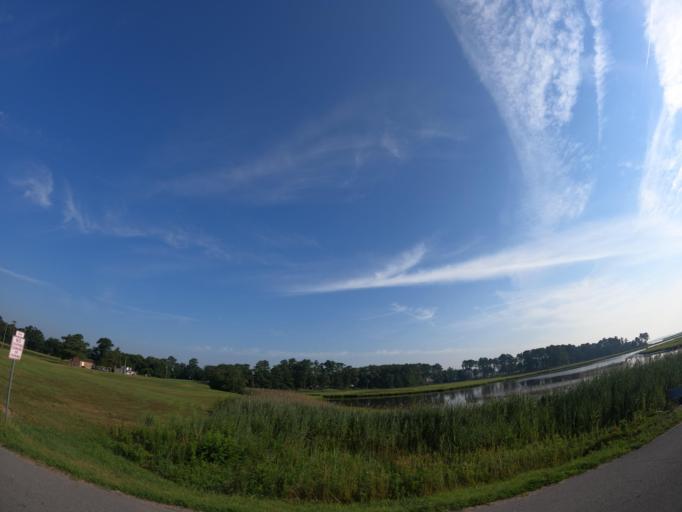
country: US
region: Delaware
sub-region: Sussex County
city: Long Neck
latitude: 38.5556
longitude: -75.2044
